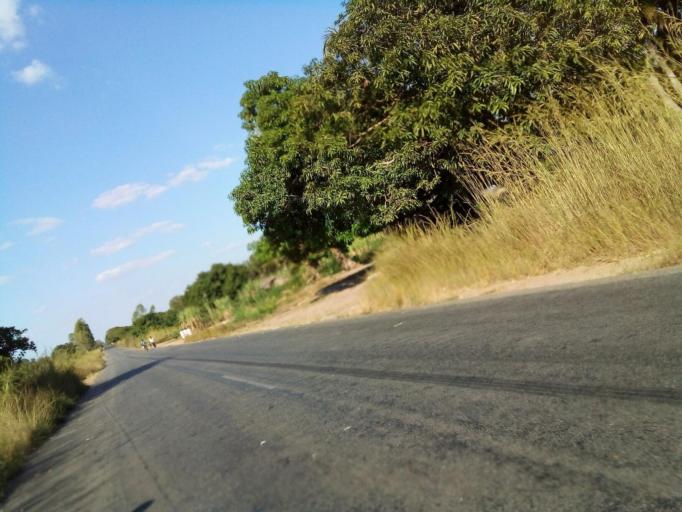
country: MZ
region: Zambezia
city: Quelimane
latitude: -17.5756
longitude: 36.6305
